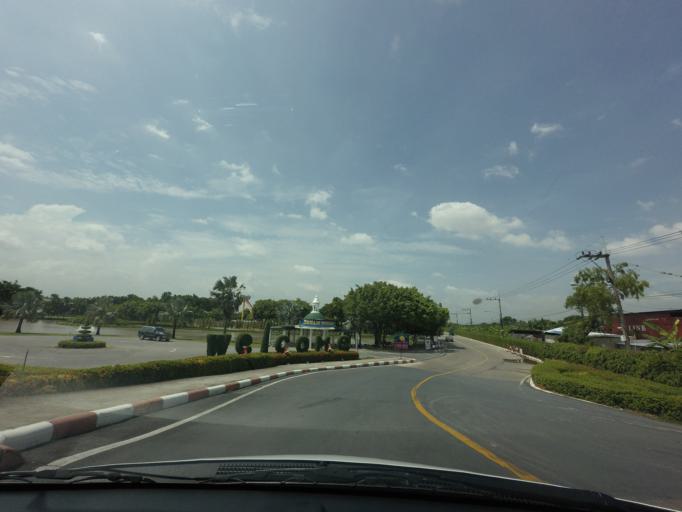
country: TH
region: Pathum Thani
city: Thanyaburi
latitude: 13.9966
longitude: 100.6749
